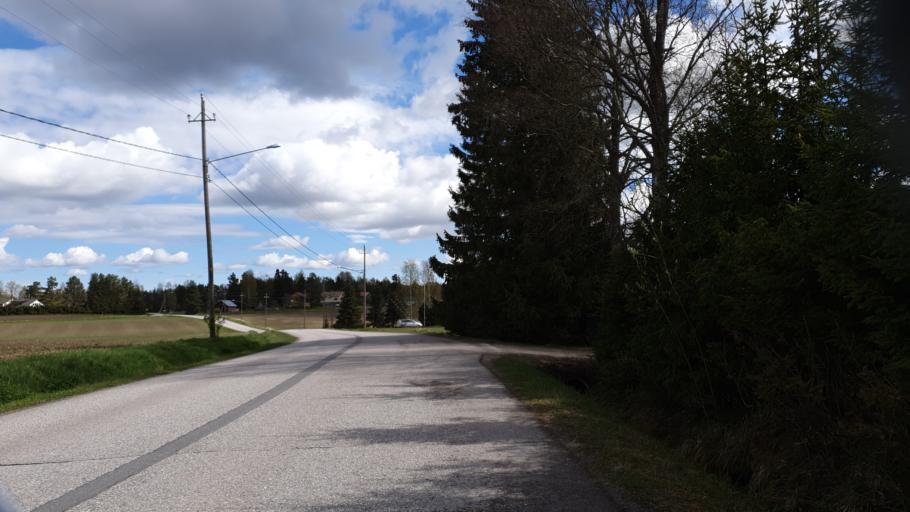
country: FI
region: Uusimaa
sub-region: Helsinki
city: Tuusula
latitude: 60.3966
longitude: 24.9208
